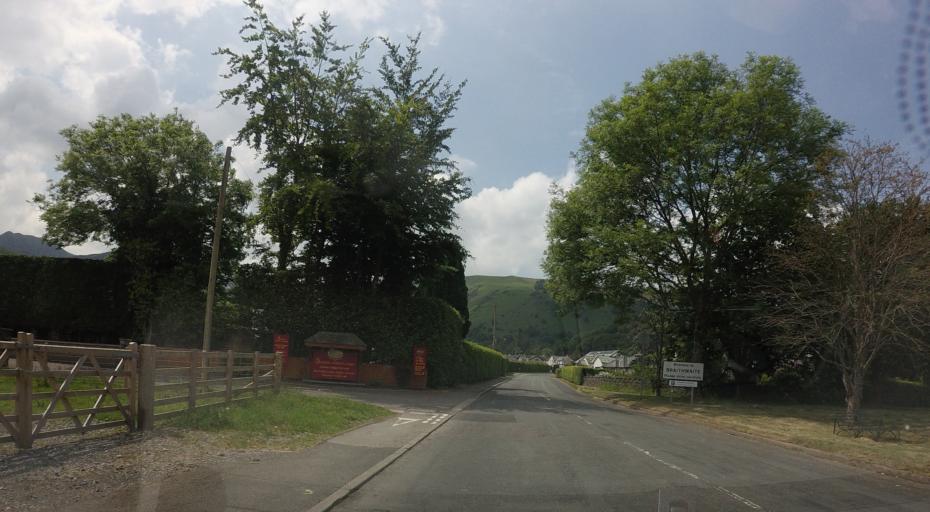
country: GB
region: England
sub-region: Cumbria
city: Keswick
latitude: 54.6022
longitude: -3.1849
